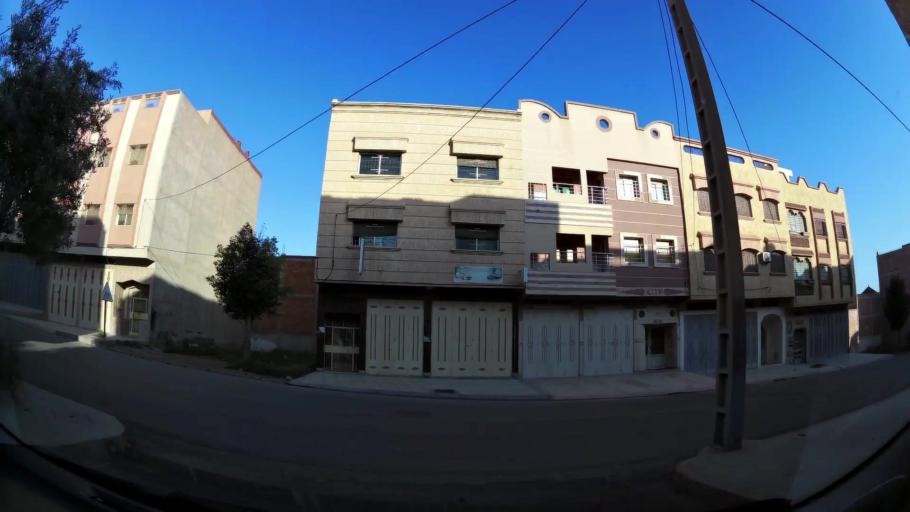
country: MA
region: Oriental
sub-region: Oujda-Angad
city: Oujda
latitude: 34.6763
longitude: -1.9404
